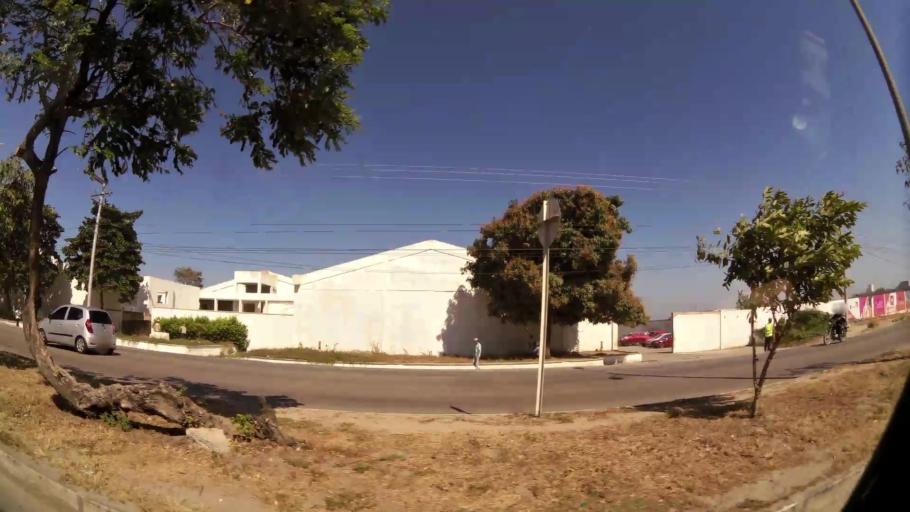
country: CO
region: Atlantico
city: Barranquilla
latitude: 10.9447
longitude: -74.7841
